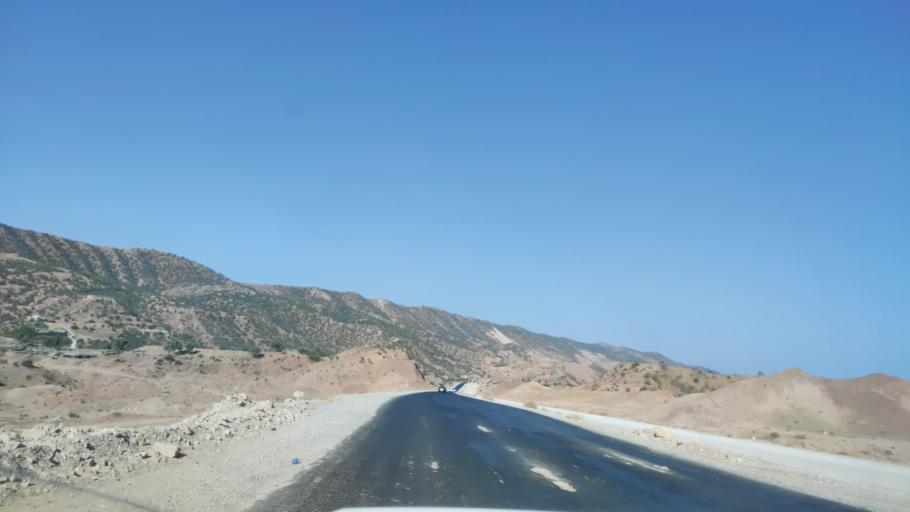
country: IQ
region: Arbil
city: Shaqlawah
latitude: 36.4298
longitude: 44.3361
